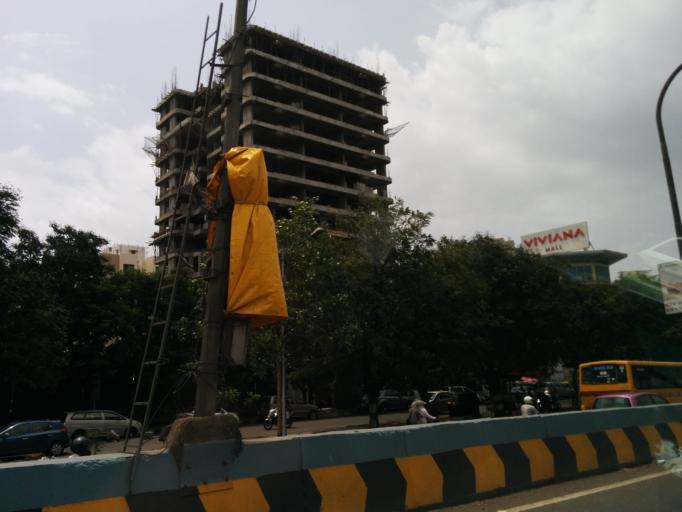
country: IN
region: Maharashtra
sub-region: Thane
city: Thane
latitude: 19.2067
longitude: 72.9710
